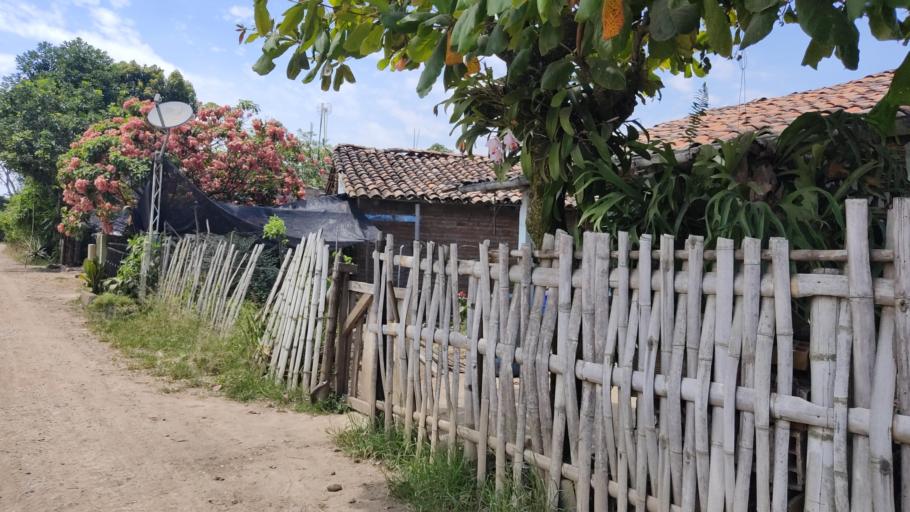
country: CO
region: Valle del Cauca
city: Jamundi
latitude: 3.1624
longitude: -76.5116
